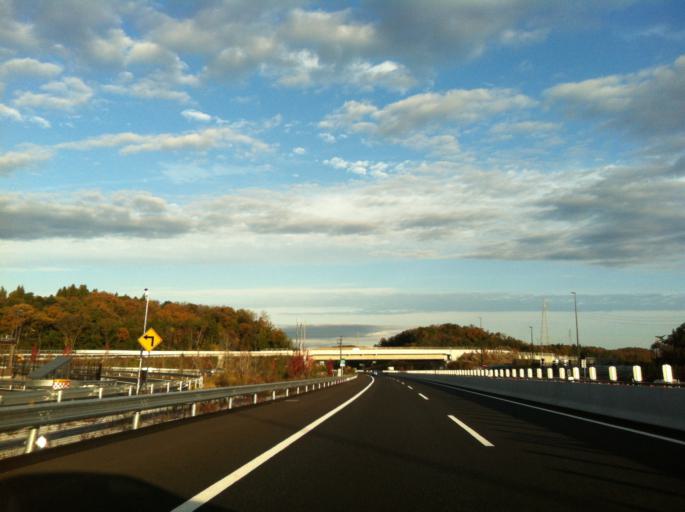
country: JP
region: Aichi
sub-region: Toyota-shi
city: Toyota
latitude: 35.0298
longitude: 137.2224
